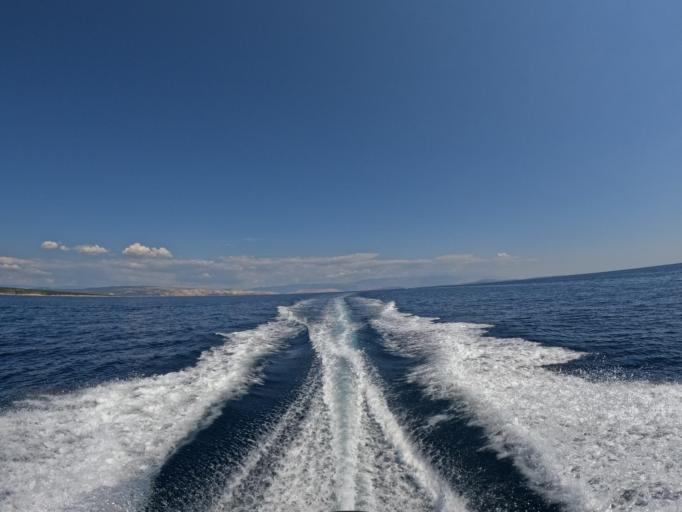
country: HR
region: Primorsko-Goranska
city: Cres
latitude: 44.9375
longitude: 14.5014
